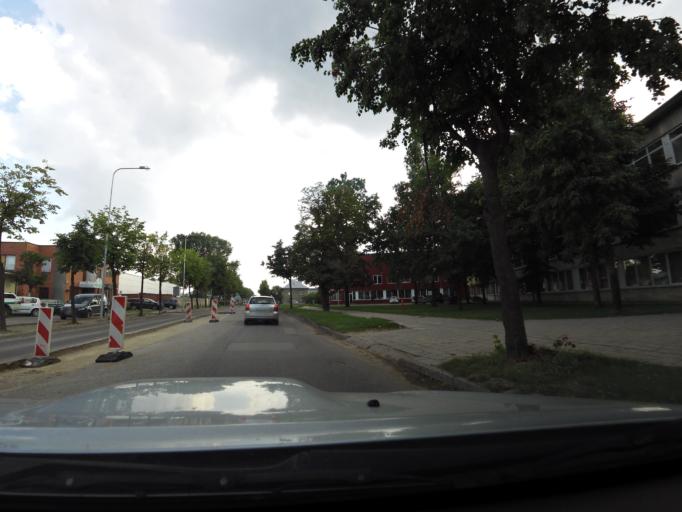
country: LT
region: Siauliu apskritis
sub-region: Siauliai
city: Siauliai
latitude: 55.9530
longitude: 23.3148
